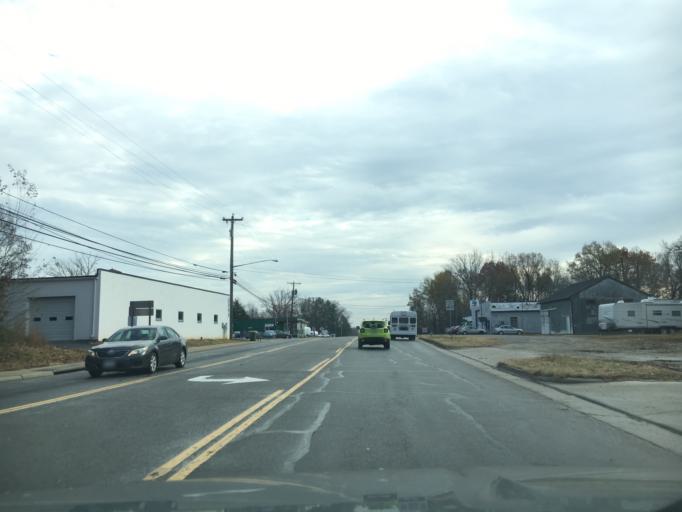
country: US
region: Virginia
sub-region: Prince Edward County
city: Farmville
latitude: 37.3122
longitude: -78.4213
